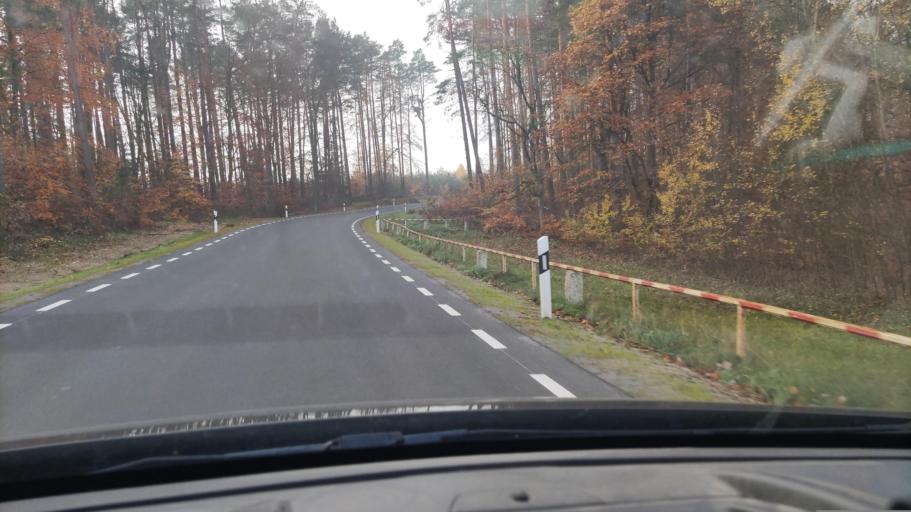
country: DE
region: Brandenburg
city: Furstenberg
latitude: 53.2381
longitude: 13.0848
